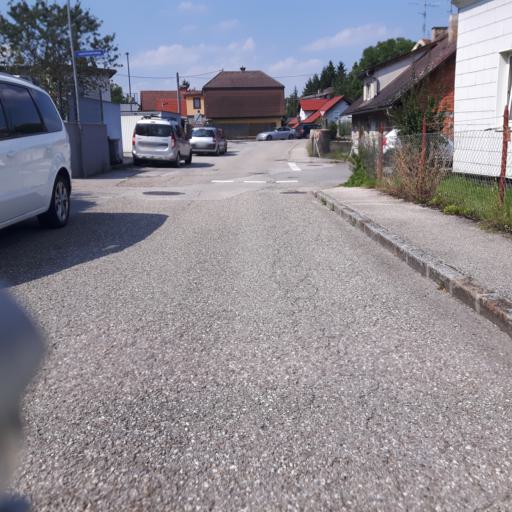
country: AT
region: Upper Austria
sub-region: Wels-Land
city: Stadl-Paura
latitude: 48.0843
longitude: 13.8665
